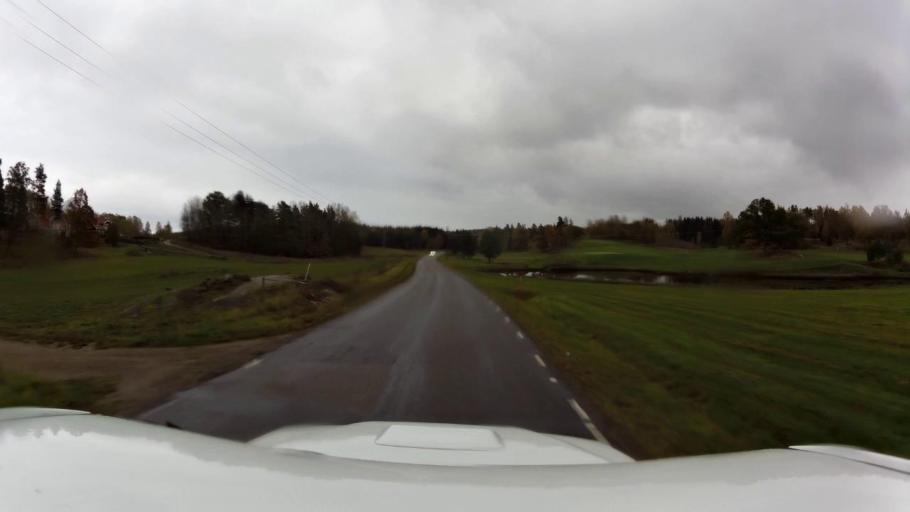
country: SE
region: OEstergoetland
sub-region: Linkopings Kommun
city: Ljungsbro
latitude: 58.5258
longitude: 15.5222
